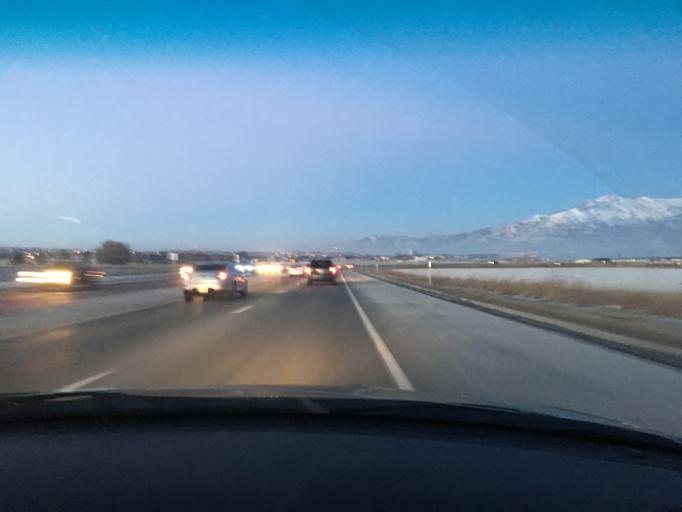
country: US
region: Utah
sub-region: Utah County
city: Saratoga Springs
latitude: 40.3852
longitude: -111.9293
